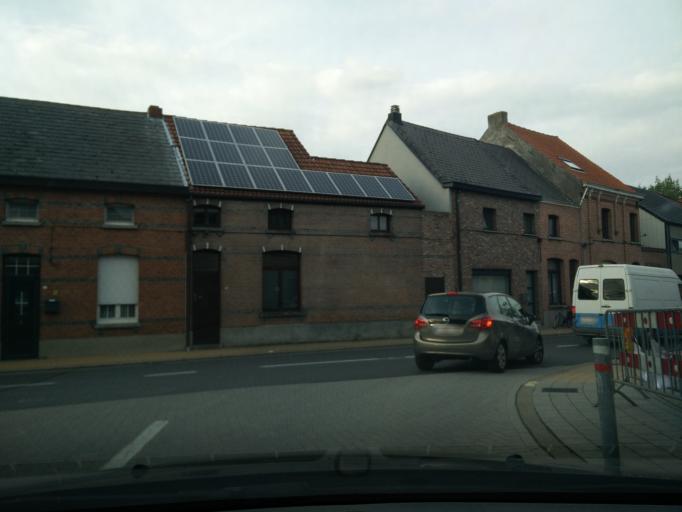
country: BE
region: Flanders
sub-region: Provincie Antwerpen
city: Bornem
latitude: 51.0930
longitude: 4.2224
